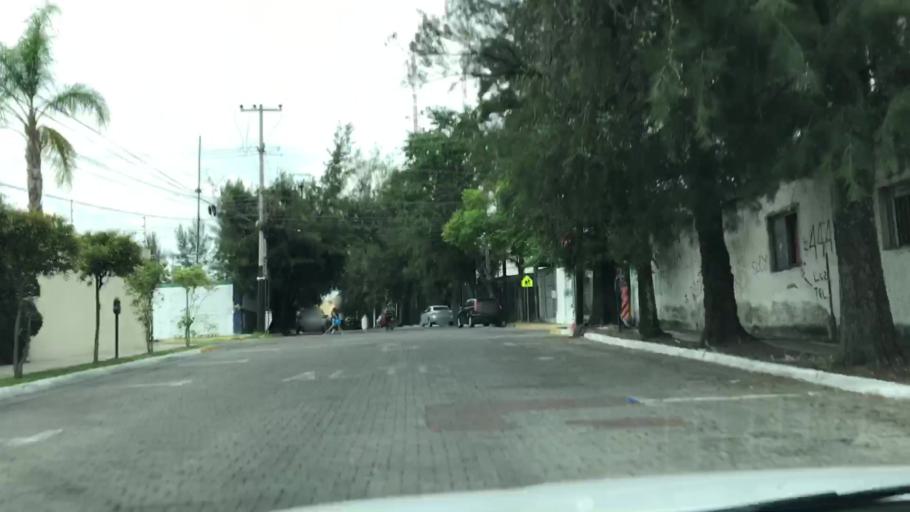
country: MX
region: Jalisco
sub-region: Zapopan
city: Zapopan
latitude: 20.7177
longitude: -103.3893
